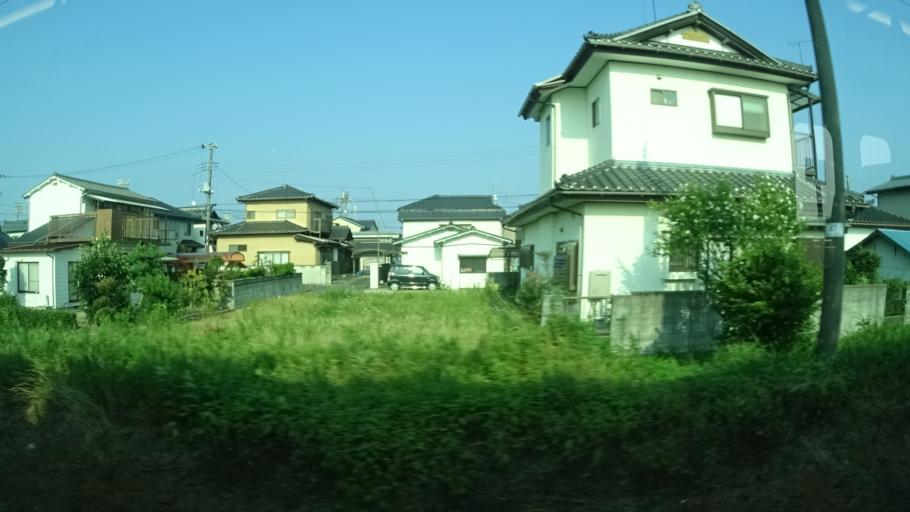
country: JP
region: Ibaraki
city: Takahagi
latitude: 36.7066
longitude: 140.7163
